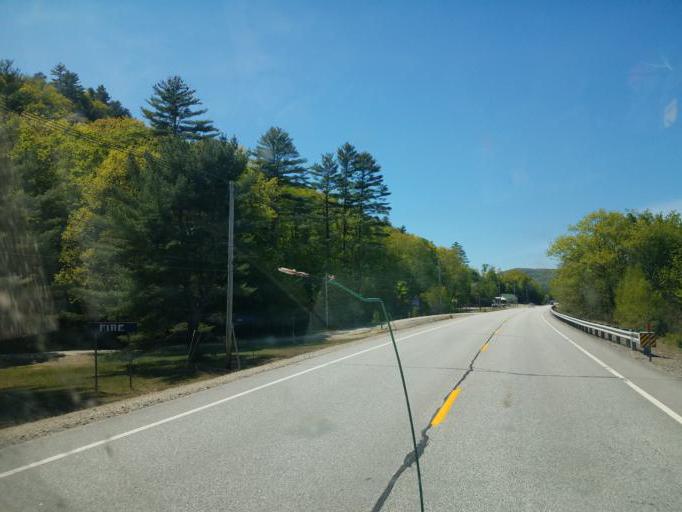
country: US
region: New Hampshire
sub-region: Grafton County
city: Rumney
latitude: 43.7841
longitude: -71.7852
